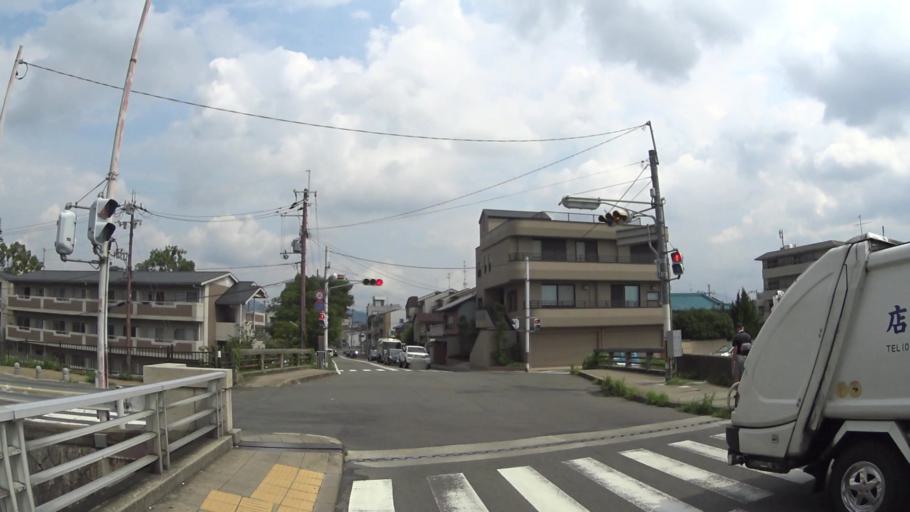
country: JP
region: Kyoto
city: Muko
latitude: 34.9998
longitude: 135.7049
